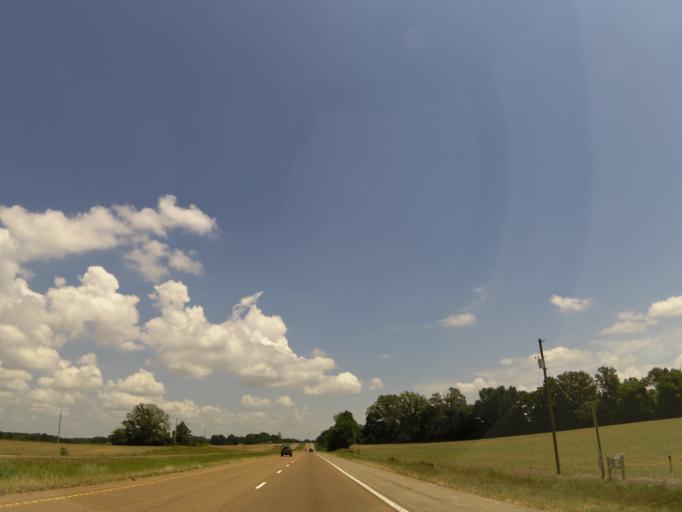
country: US
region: Tennessee
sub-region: Lauderdale County
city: Halls
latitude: 35.9449
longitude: -89.3045
